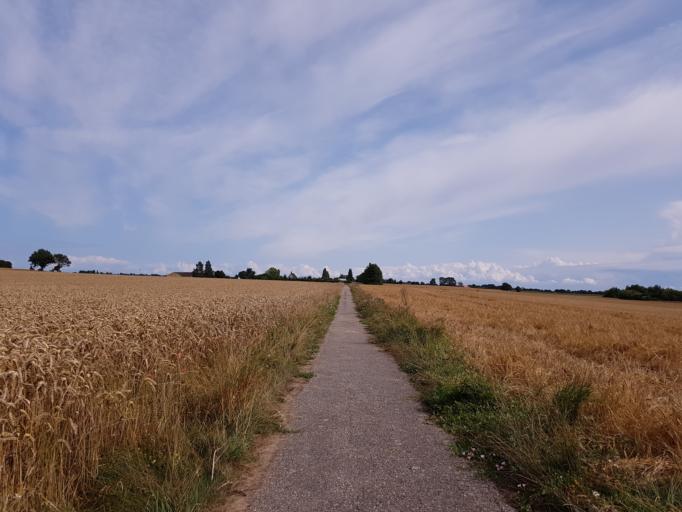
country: DK
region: Zealand
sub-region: Guldborgsund Kommune
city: Nykobing Falster
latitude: 54.5875
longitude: 11.9366
